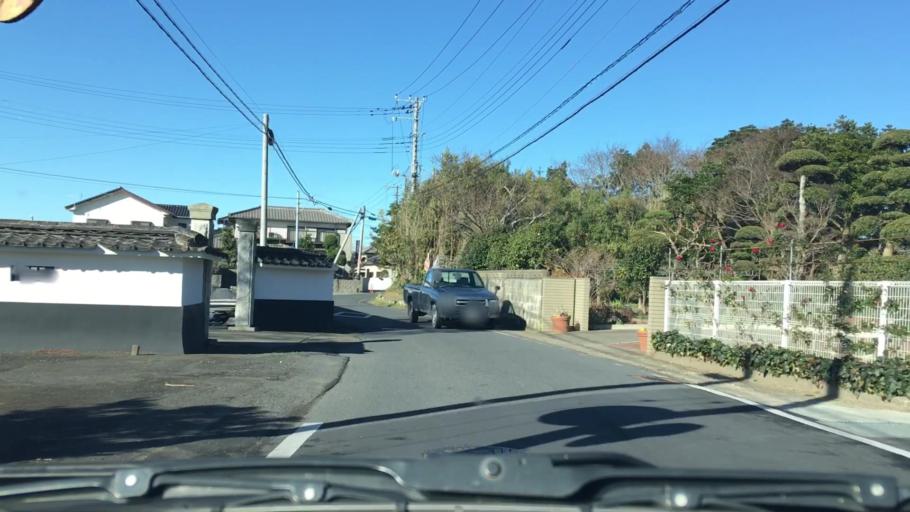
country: JP
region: Chiba
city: Omigawa
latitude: 35.8649
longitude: 140.6660
